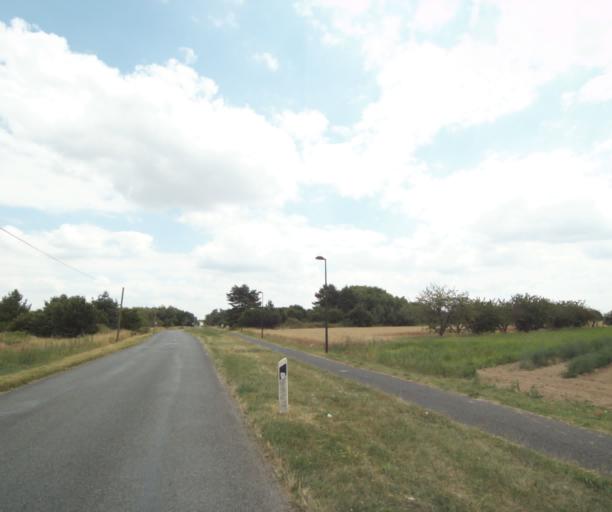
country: FR
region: Centre
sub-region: Departement du Loiret
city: Saint-Pryve-Saint-Mesmin
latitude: 47.8595
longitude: 1.8716
